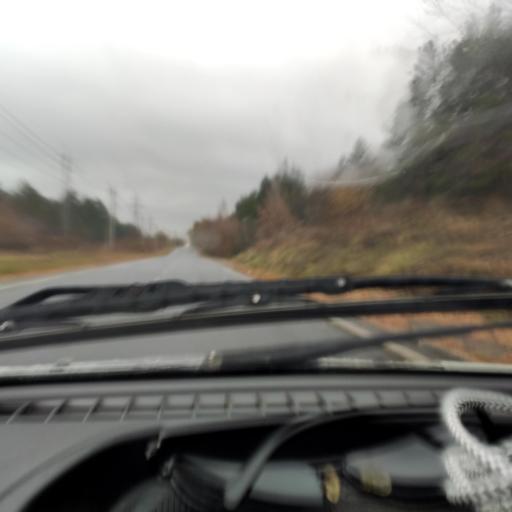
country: RU
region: Samara
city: Zhigulevsk
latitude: 53.5063
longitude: 49.4581
